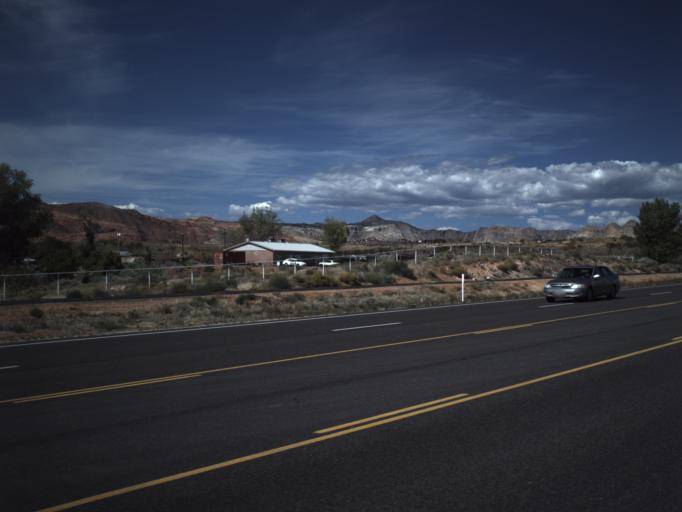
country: US
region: Utah
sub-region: Washington County
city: Ivins
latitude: 37.1850
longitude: -113.6192
